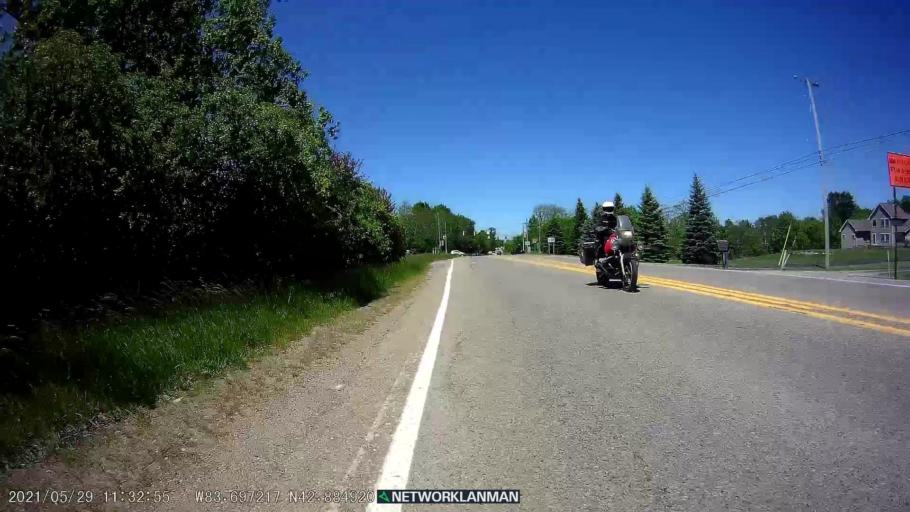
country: US
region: Michigan
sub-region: Genesee County
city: Lake Fenton
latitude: 42.8843
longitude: -83.6973
